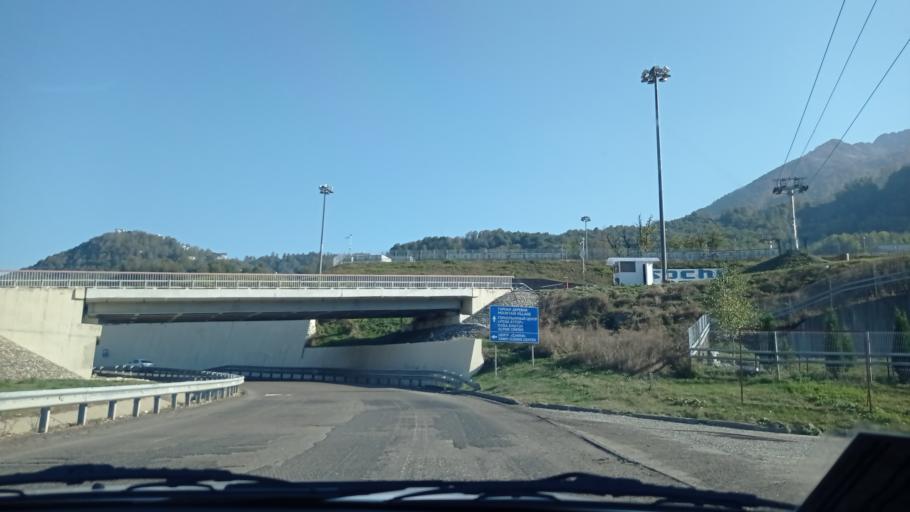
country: RU
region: Krasnodarskiy
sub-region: Sochi City
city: Krasnaya Polyana
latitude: 43.6712
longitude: 40.2872
